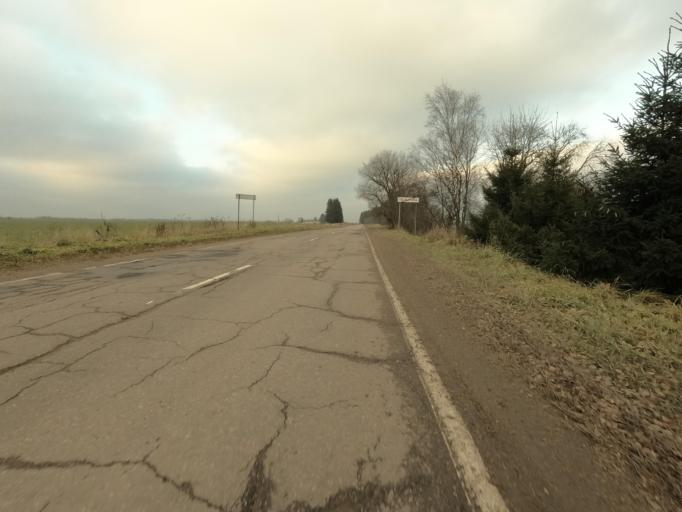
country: RU
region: Leningrad
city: Mga
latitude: 59.7768
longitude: 31.0245
